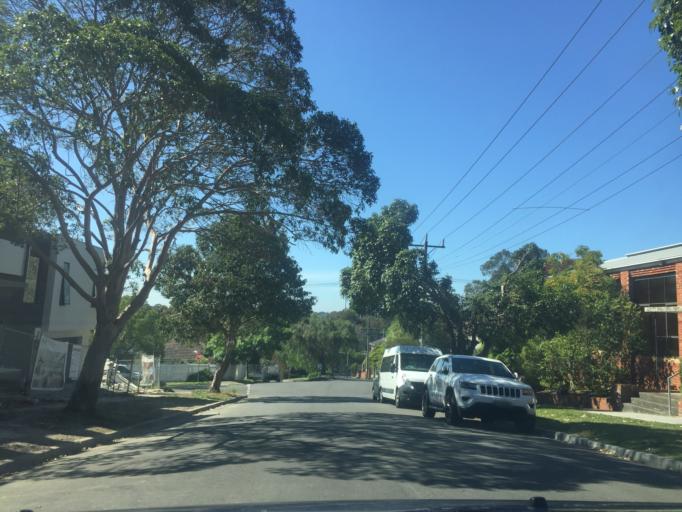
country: AU
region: Victoria
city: Alphington
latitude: -37.7928
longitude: 145.0353
